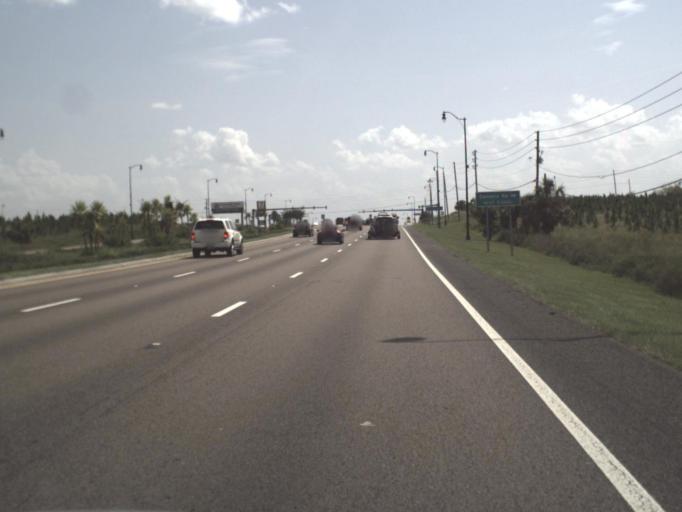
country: US
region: Florida
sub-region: Polk County
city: Davenport
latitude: 28.1609
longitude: -81.6399
